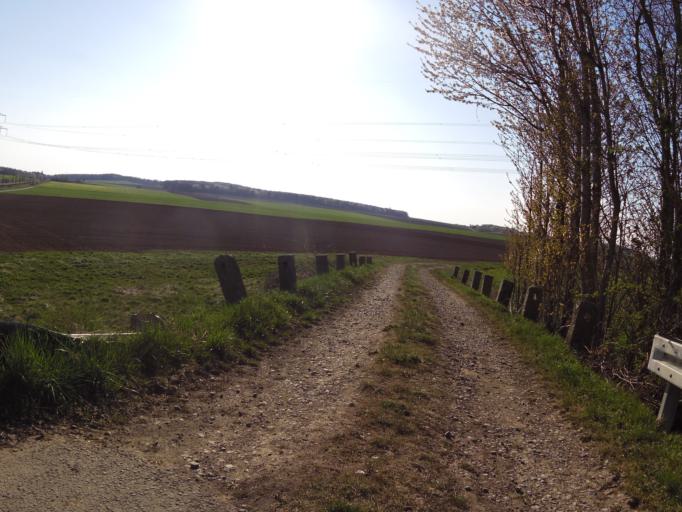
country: DE
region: Bavaria
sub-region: Regierungsbezirk Unterfranken
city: Oberpleichfeld
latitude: 49.8346
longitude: 10.0922
